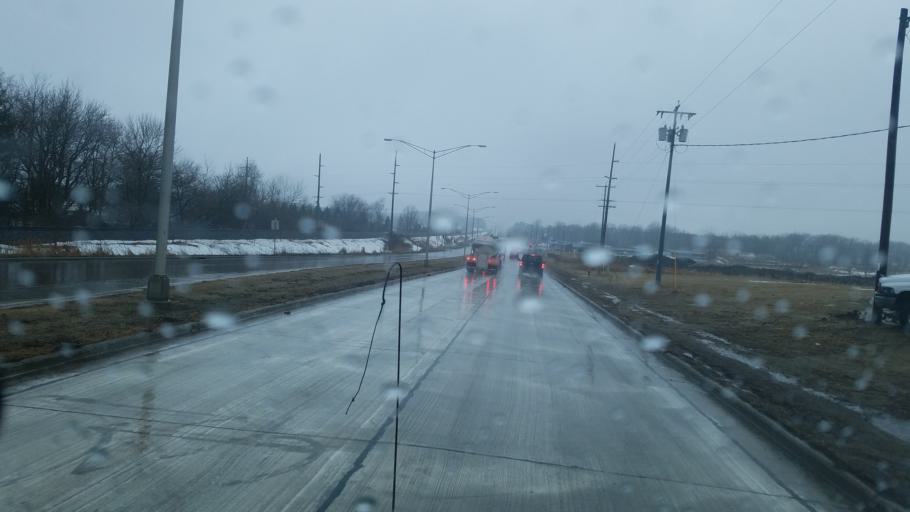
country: US
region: Wisconsin
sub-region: Wood County
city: Marshfield
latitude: 44.6843
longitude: -90.1955
